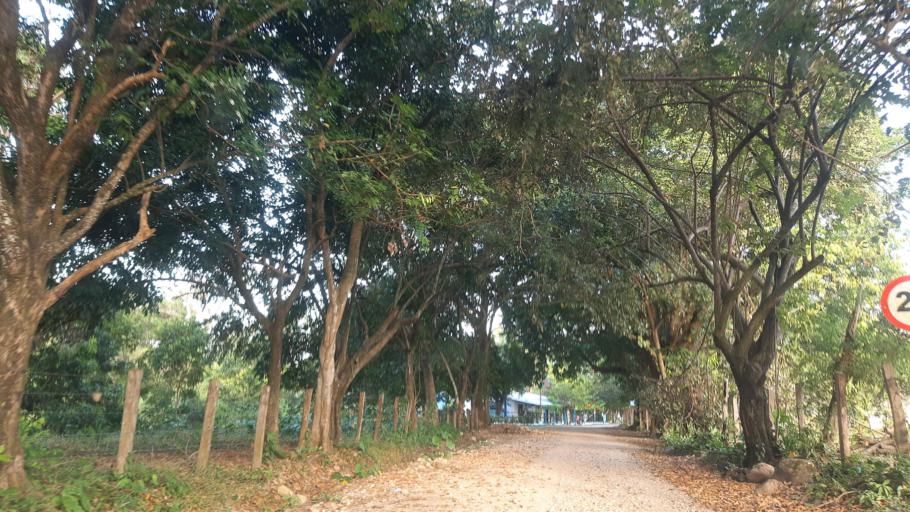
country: CO
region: Arauca
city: Tame
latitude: 6.4992
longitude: -71.7667
